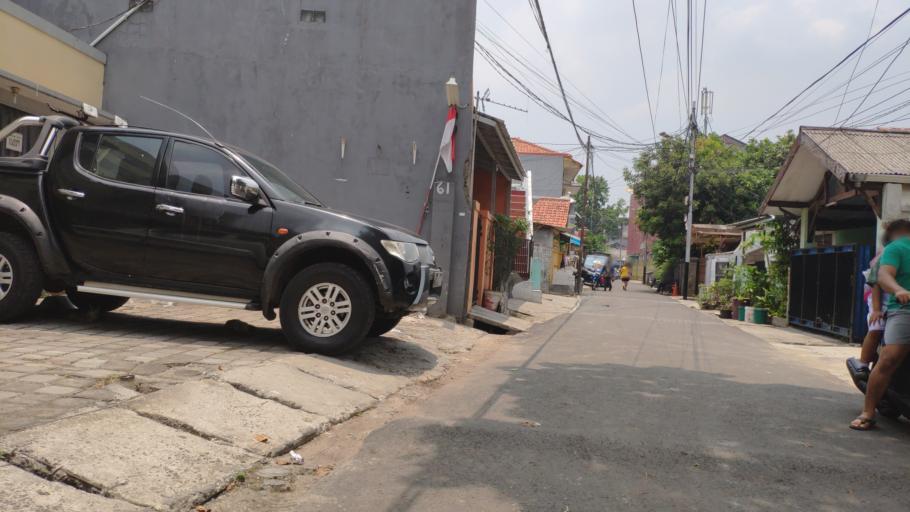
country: ID
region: Jakarta Raya
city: Jakarta
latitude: -6.2660
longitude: 106.7926
